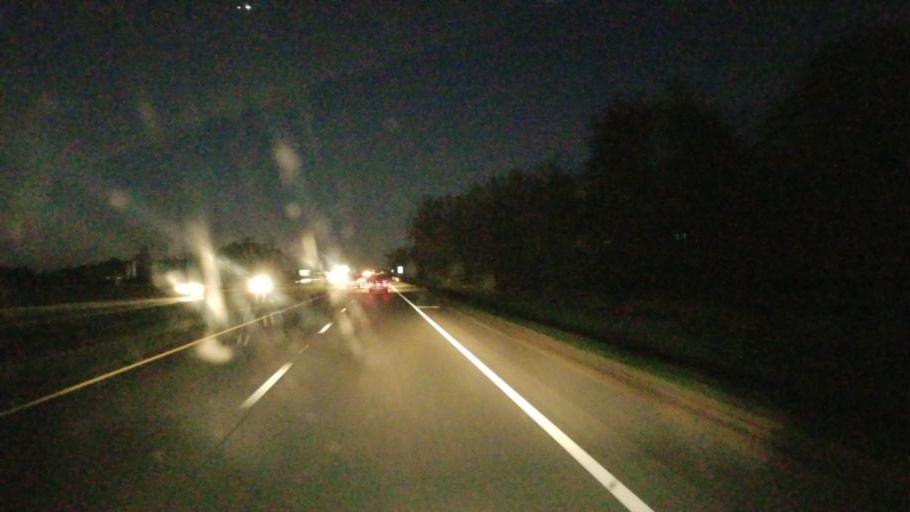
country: US
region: Ohio
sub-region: Pickaway County
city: Circleville
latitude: 39.6421
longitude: -82.9566
